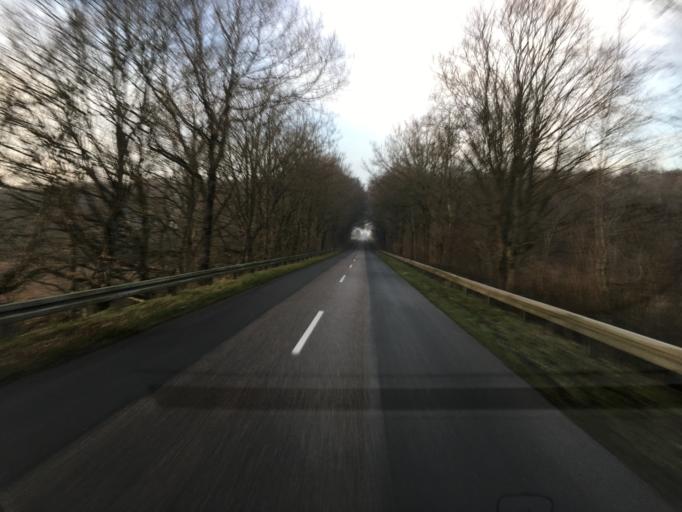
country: DK
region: South Denmark
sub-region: Tonder Kommune
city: Toftlund
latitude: 55.1413
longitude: 9.0537
